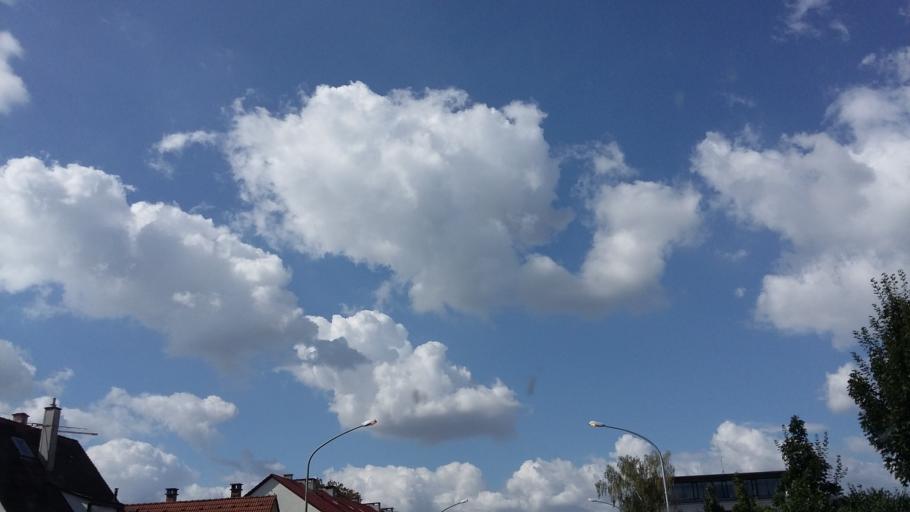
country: DE
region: Bavaria
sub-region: Swabia
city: Neu-Ulm
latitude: 48.3890
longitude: 10.0151
